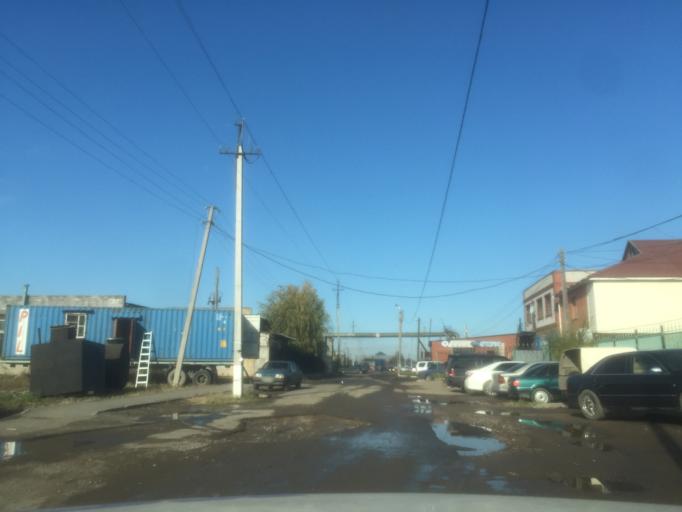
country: KZ
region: Astana Qalasy
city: Astana
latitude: 51.1831
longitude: 71.3881
